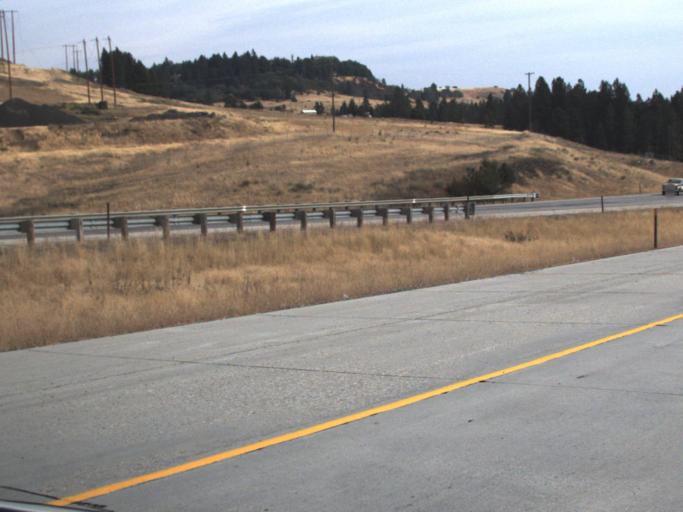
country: US
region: Washington
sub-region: Spokane County
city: Mead
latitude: 47.7343
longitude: -117.3585
